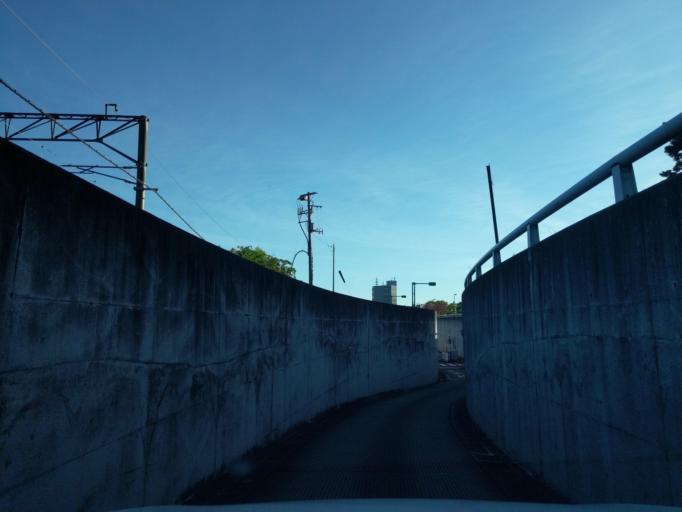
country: JP
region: Fukushima
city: Koriyama
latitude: 37.3690
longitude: 140.3747
